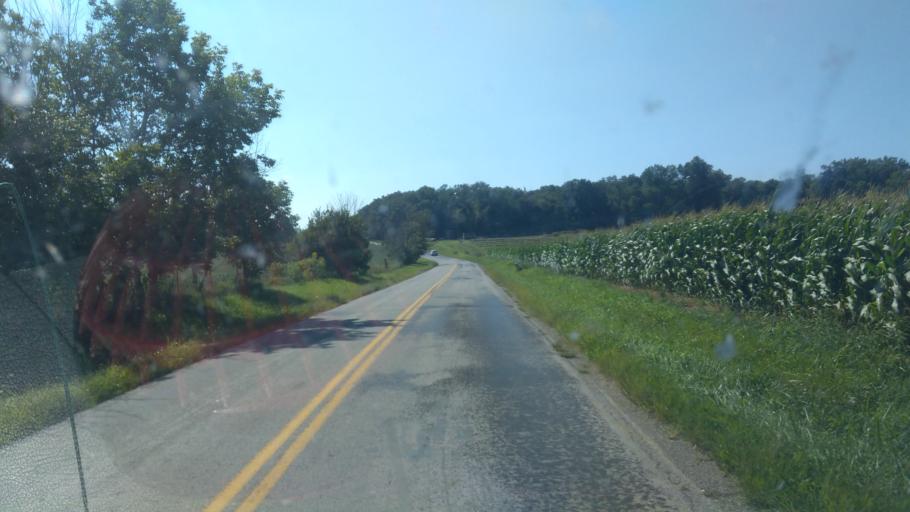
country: US
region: Ohio
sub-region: Ashland County
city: Ashland
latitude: 40.9709
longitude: -82.3236
